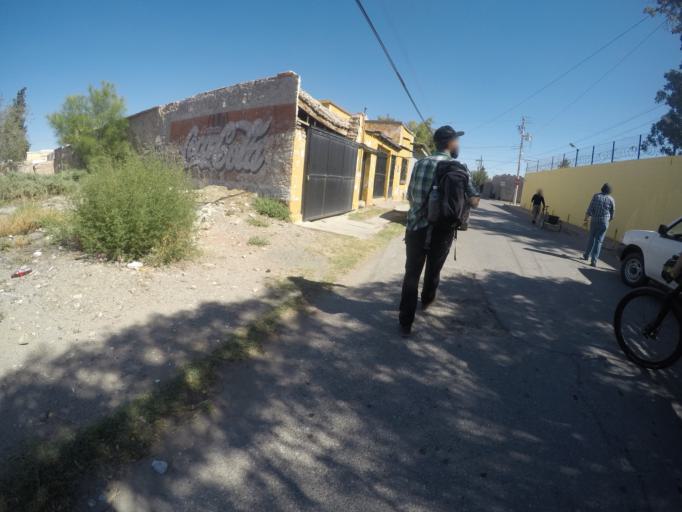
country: MX
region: Chihuahua
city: Ciudad Juarez
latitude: 31.7395
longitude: -106.4725
